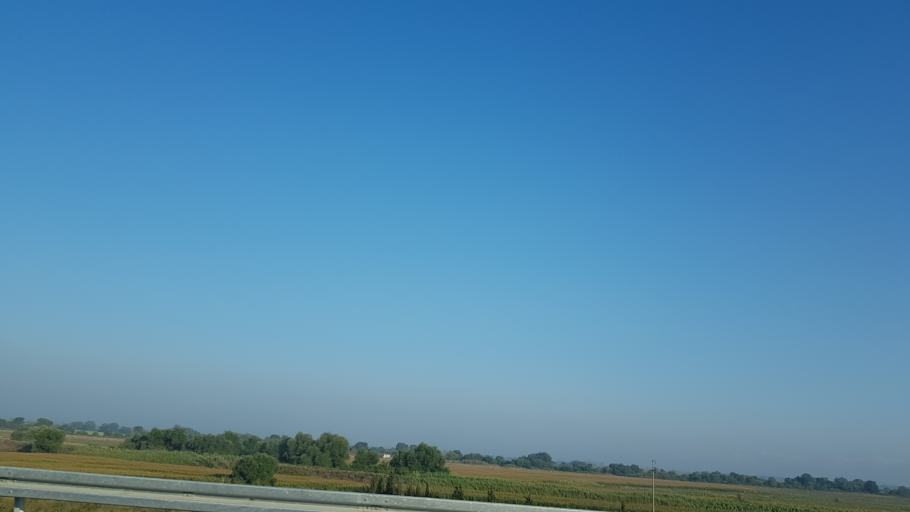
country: TR
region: Bursa
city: Karacabey
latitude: 40.1242
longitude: 28.2839
